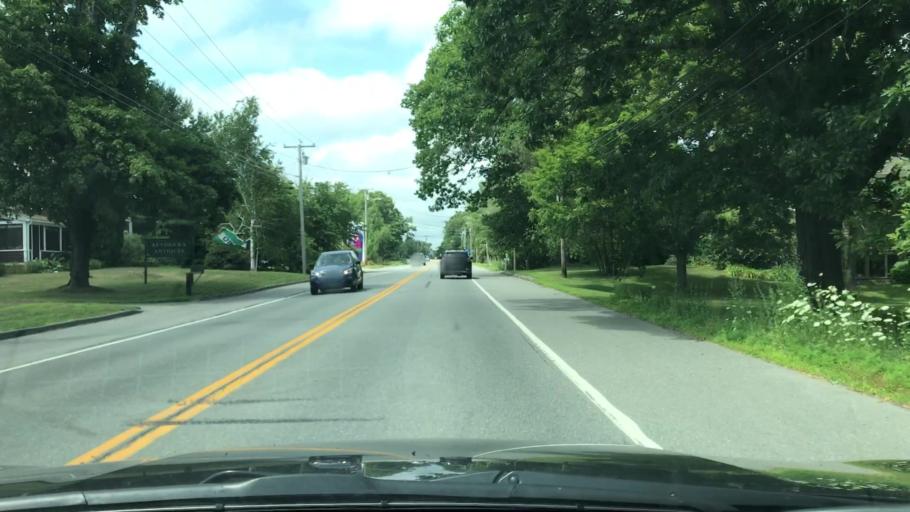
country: US
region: Maine
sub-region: Waldo County
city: Belfast
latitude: 44.4042
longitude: -68.9901
